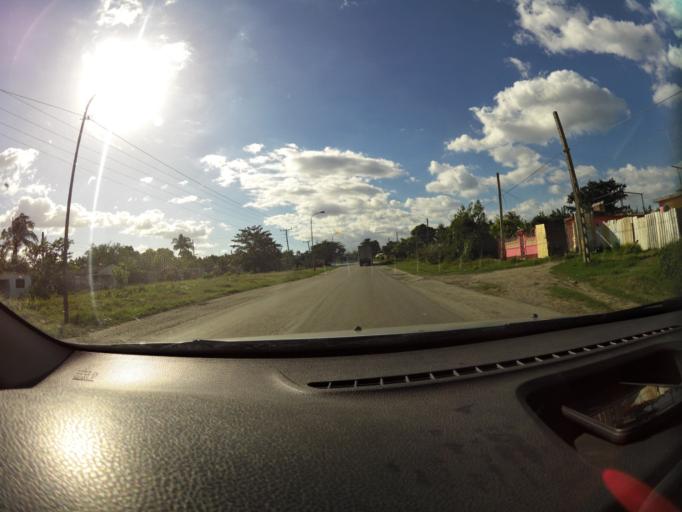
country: CU
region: Santiago de Cuba
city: Palma Soriano
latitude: 20.2321
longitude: -76.0154
